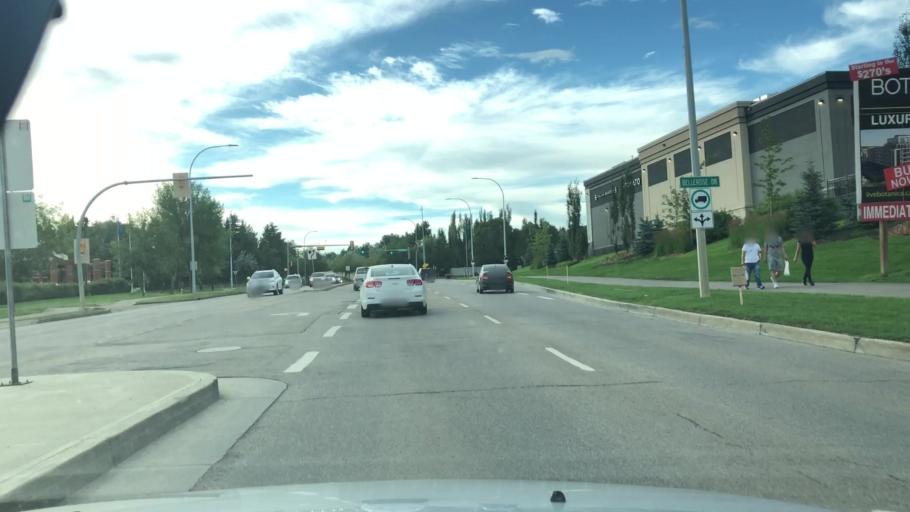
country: CA
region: Alberta
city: St. Albert
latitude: 53.6493
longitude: -113.6164
